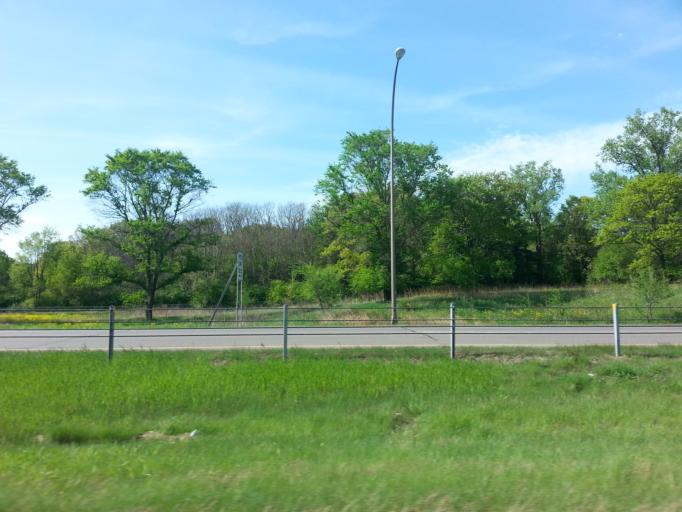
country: US
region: Minnesota
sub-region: Ramsey County
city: Little Canada
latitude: 45.0091
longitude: -93.0961
